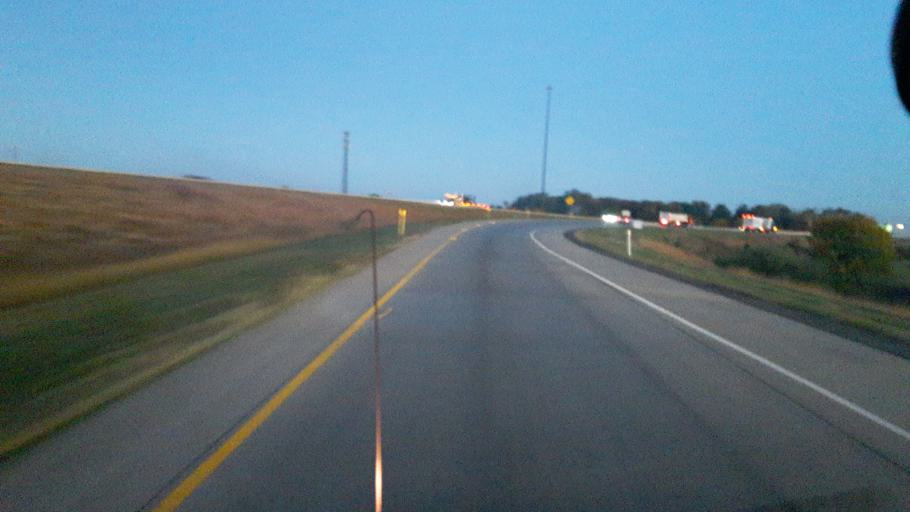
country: US
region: Indiana
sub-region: Allen County
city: New Haven
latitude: 41.0652
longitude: -84.9883
